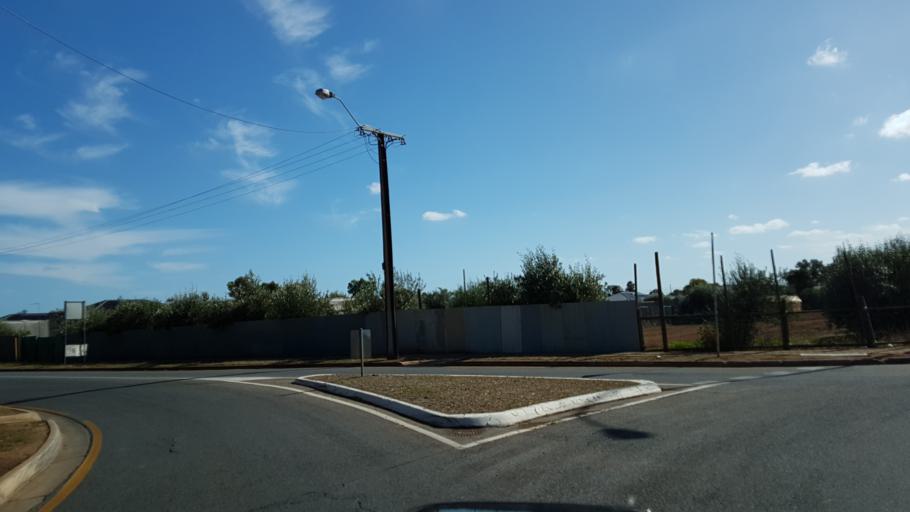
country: AU
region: South Australia
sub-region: Salisbury
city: Salisbury
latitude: -34.7353
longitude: 138.6182
